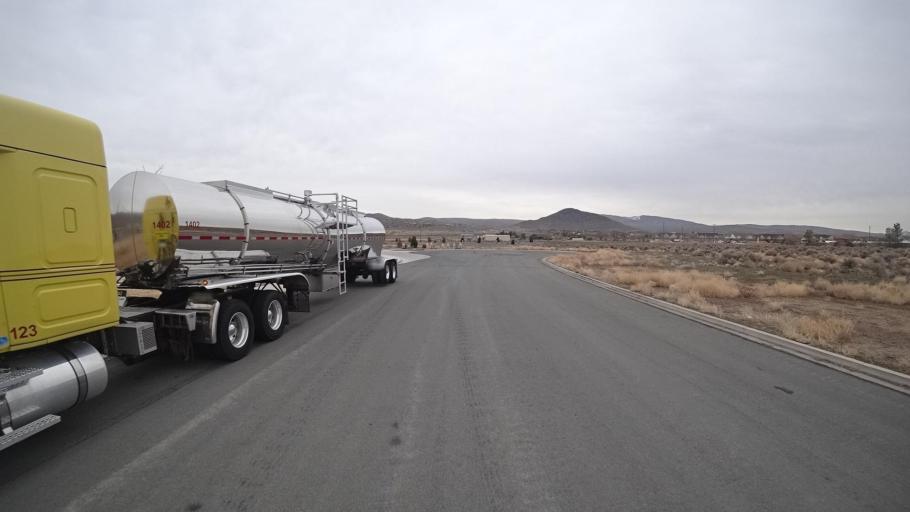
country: US
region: Nevada
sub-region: Washoe County
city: Spanish Springs
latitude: 39.6808
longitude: -119.7024
